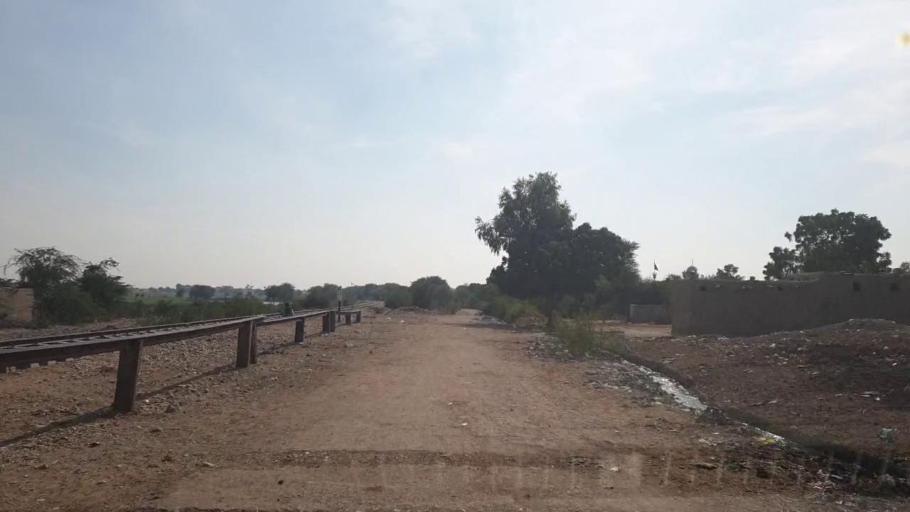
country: PK
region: Sindh
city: Hala
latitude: 25.7435
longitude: 68.2946
